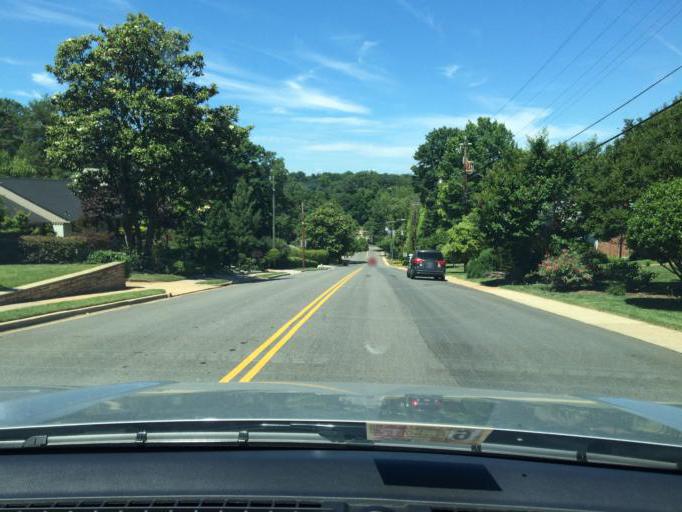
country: US
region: Virginia
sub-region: Arlington County
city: Arlington
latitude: 38.8531
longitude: -77.0706
